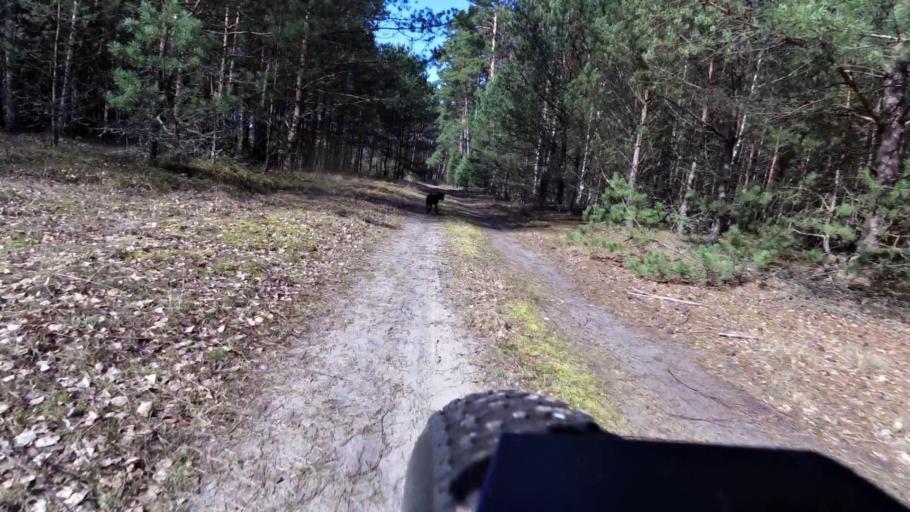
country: PL
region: Lubusz
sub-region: Powiat krosnienski
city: Maszewo
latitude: 52.2108
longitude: 14.9457
